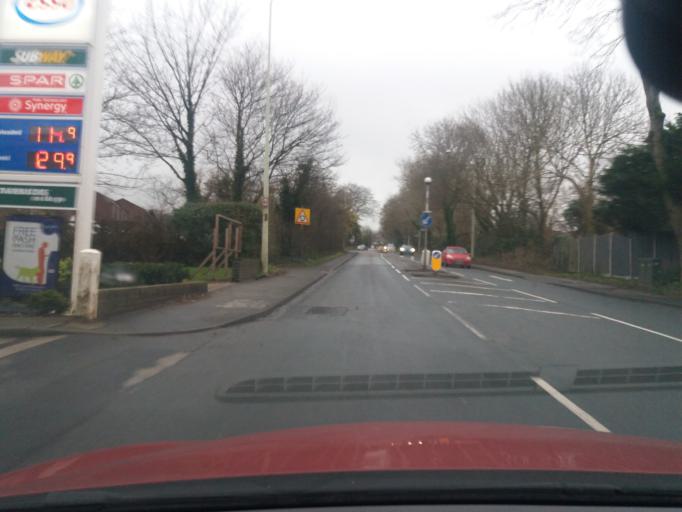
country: GB
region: England
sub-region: Lancashire
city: Clayton-le-Woods
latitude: 53.7133
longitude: -2.6454
